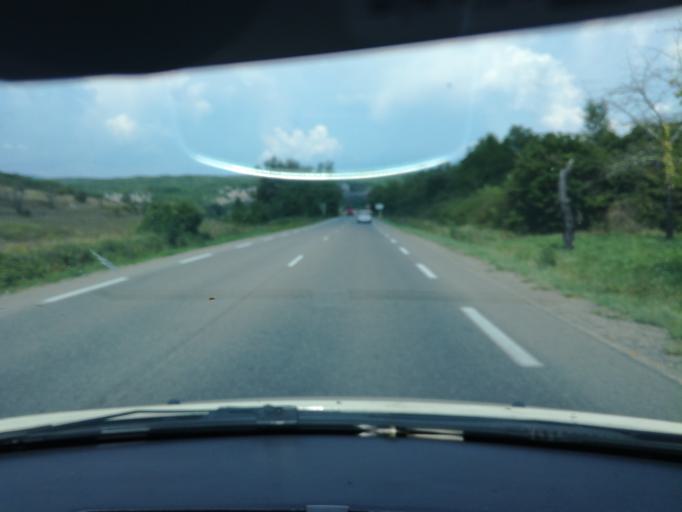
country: FR
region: Rhone-Alpes
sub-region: Departement de l'Ardeche
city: Lachapelle-sous-Aubenas
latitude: 44.5050
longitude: 4.3862
